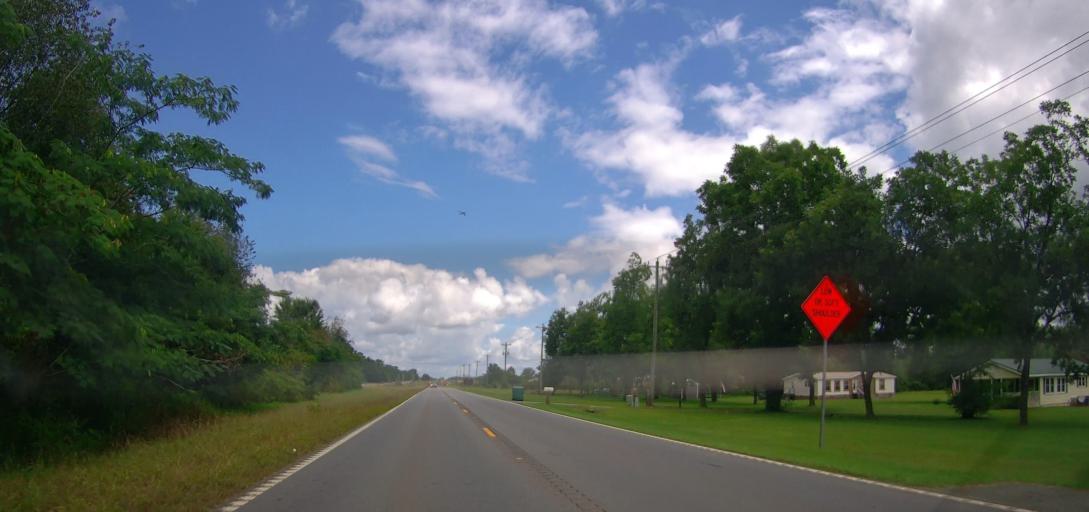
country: US
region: Georgia
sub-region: Houston County
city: Perry
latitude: 32.4608
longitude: -83.6181
